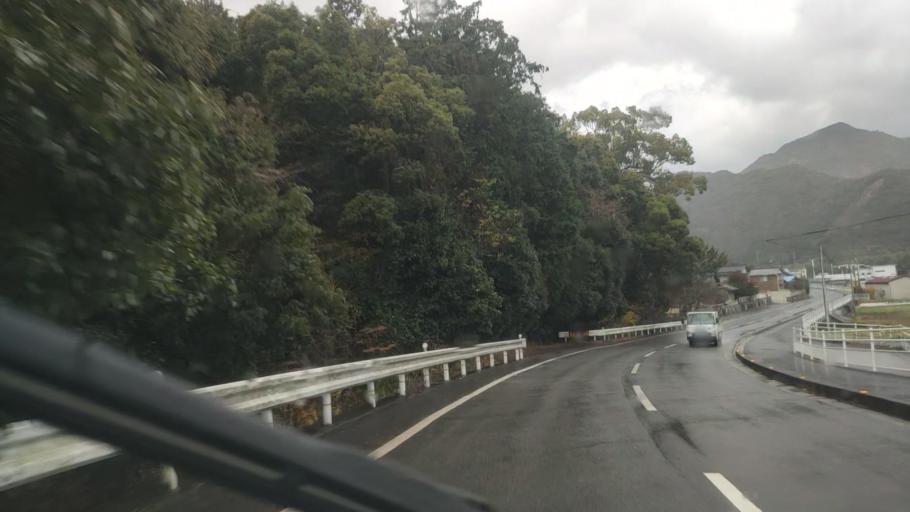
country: JP
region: Tokushima
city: Kamojimacho-jogejima
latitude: 34.2090
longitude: 134.3348
